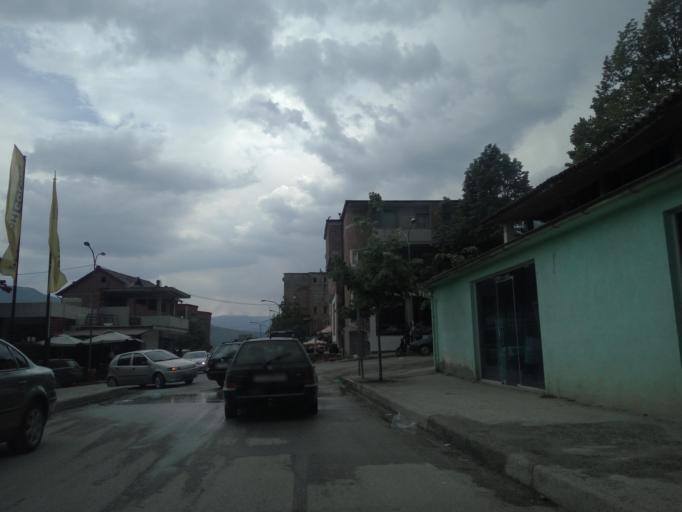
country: AL
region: Kukes
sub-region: Rrethi i Tropojes
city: Bajram Curri
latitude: 42.3572
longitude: 20.0770
